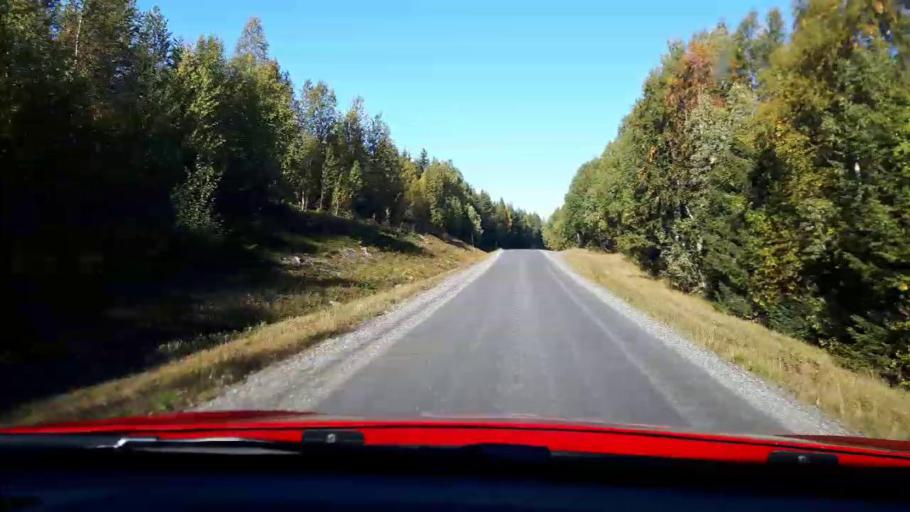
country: NO
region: Nord-Trondelag
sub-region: Lierne
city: Sandvika
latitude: 64.5368
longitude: 14.0139
